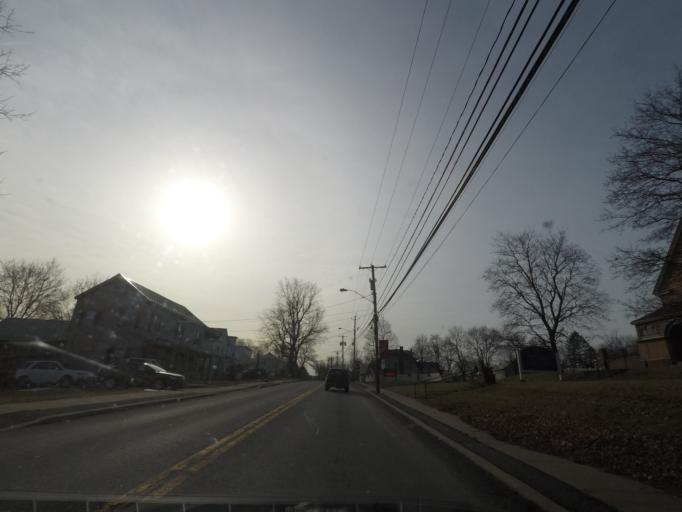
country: US
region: New York
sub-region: Saratoga County
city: Stillwater
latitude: 42.9433
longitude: -73.6480
